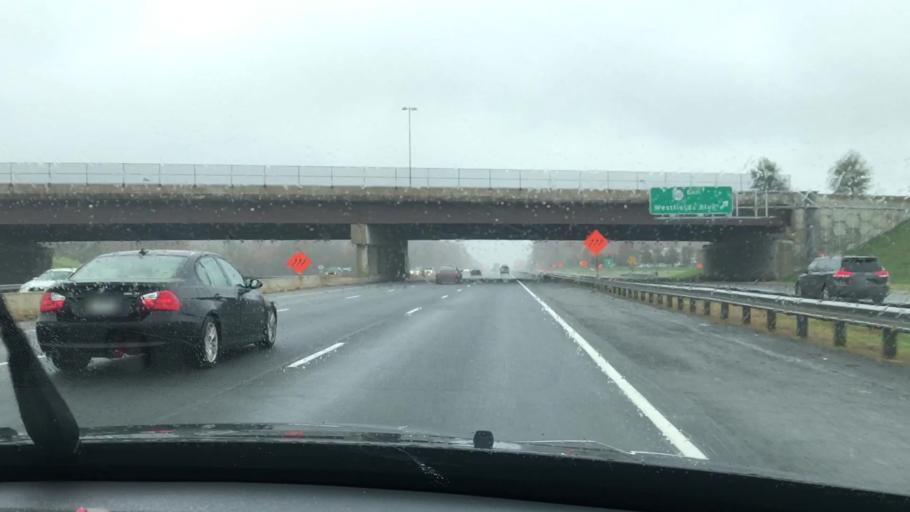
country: US
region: Virginia
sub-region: Fairfax County
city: Chantilly
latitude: 38.8737
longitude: -77.4460
